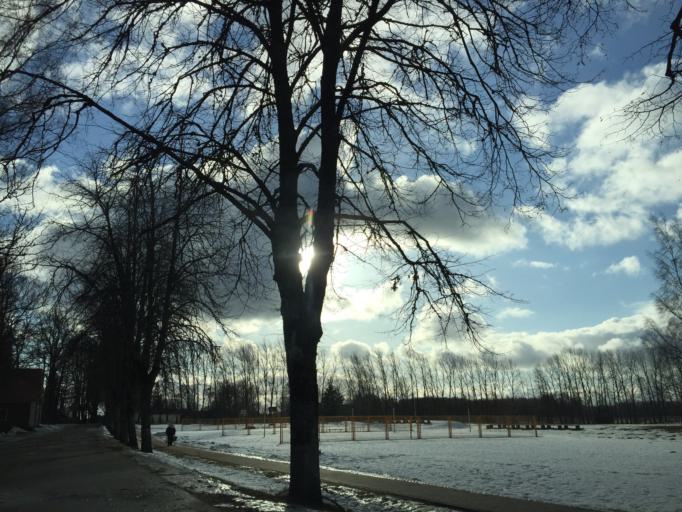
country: LV
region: Limbazu Rajons
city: Limbazi
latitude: 57.6114
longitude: 24.6089
